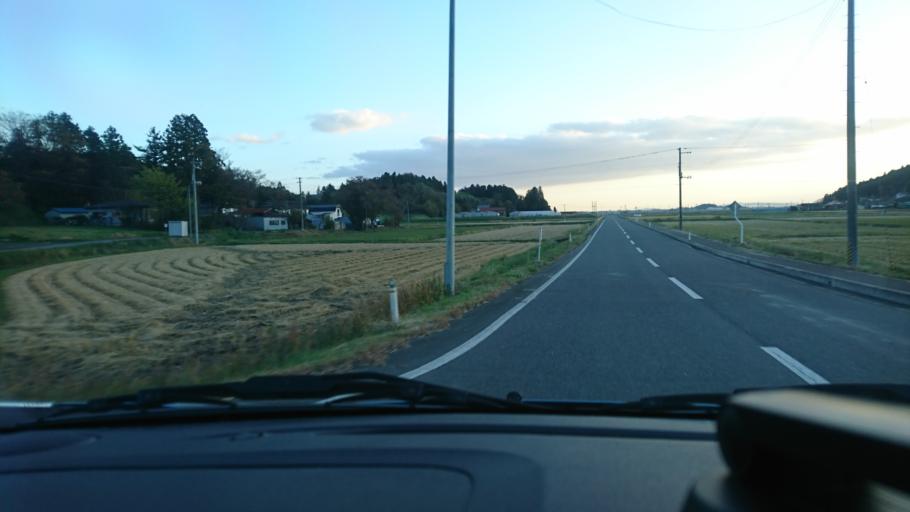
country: JP
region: Iwate
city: Ichinoseki
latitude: 38.7641
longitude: 141.2383
